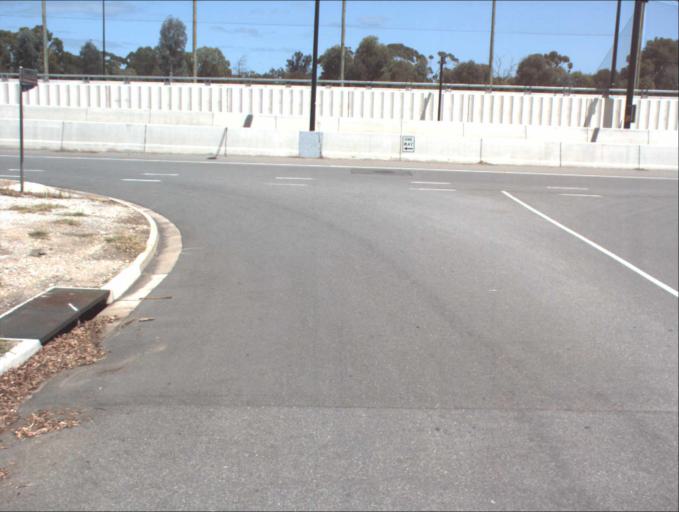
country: AU
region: South Australia
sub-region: Charles Sturt
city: Woodville North
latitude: -34.8608
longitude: 138.5682
